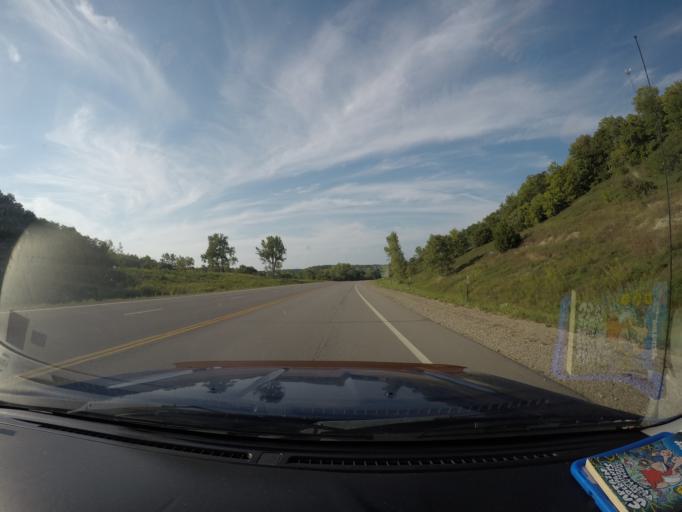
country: US
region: Kansas
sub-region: Atchison County
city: Atchison
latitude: 39.4908
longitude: -95.1312
